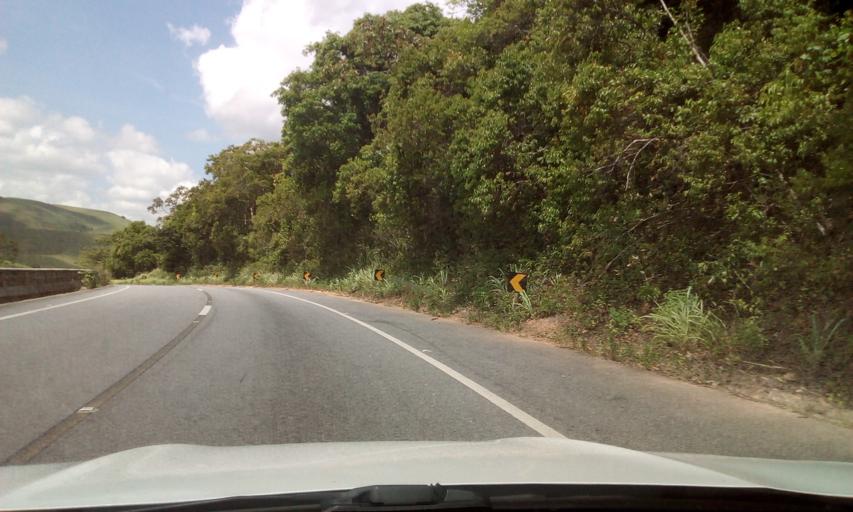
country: BR
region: Alagoas
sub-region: Flexeiras
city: Flexeiras
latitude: -9.2481
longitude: -35.7655
